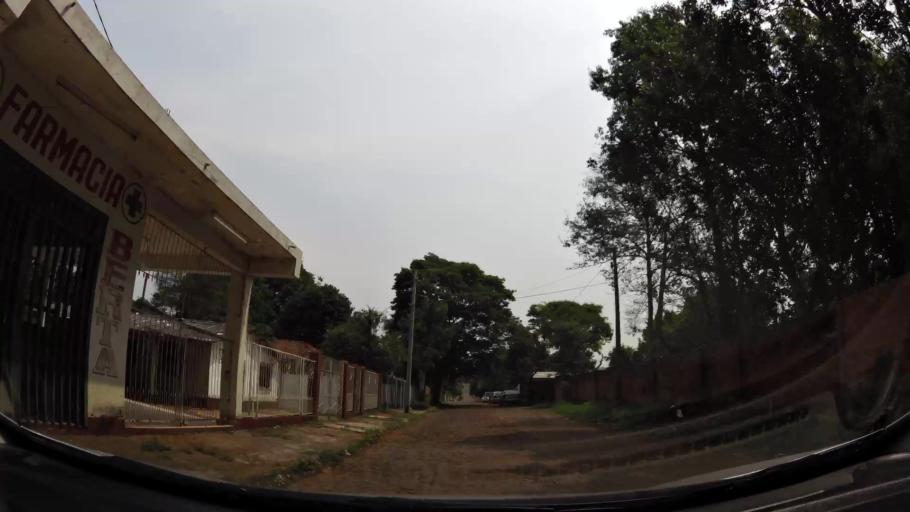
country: BR
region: Parana
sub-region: Foz Do Iguacu
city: Foz do Iguacu
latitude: -25.5648
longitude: -54.6024
